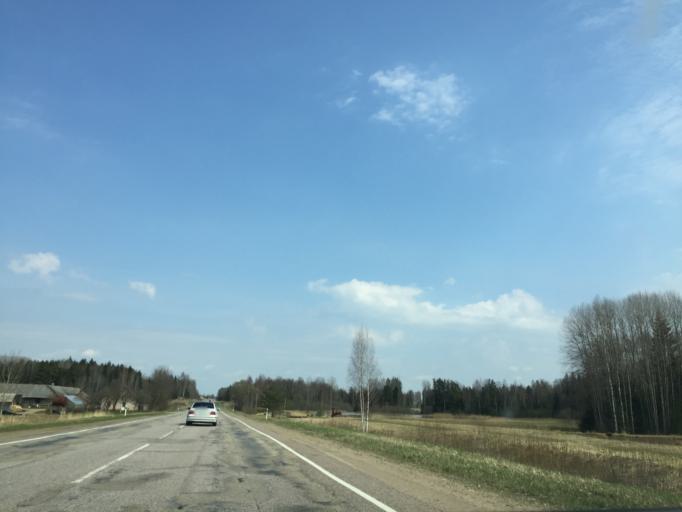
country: LV
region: Apes Novads
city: Ape
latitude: 57.4804
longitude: 26.5459
